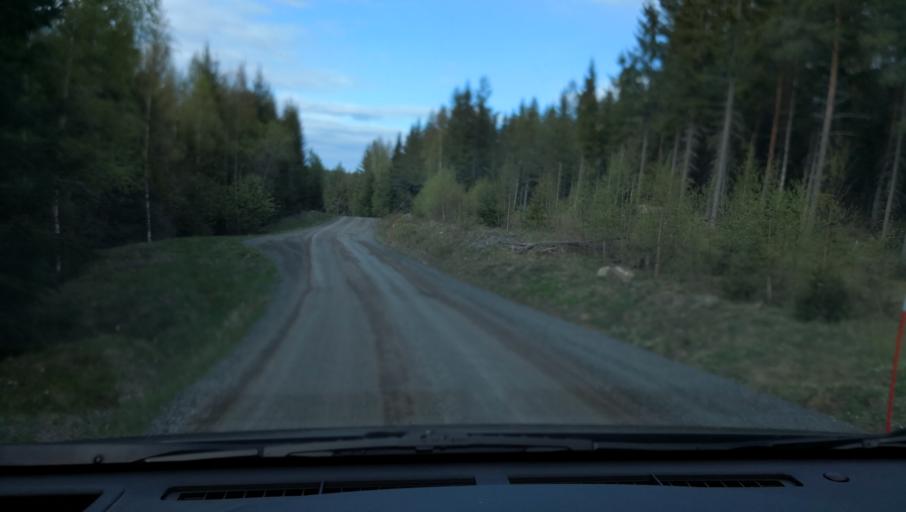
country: SE
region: Dalarna
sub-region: Saters Kommun
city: Saeter
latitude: 60.2604
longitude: 15.8244
